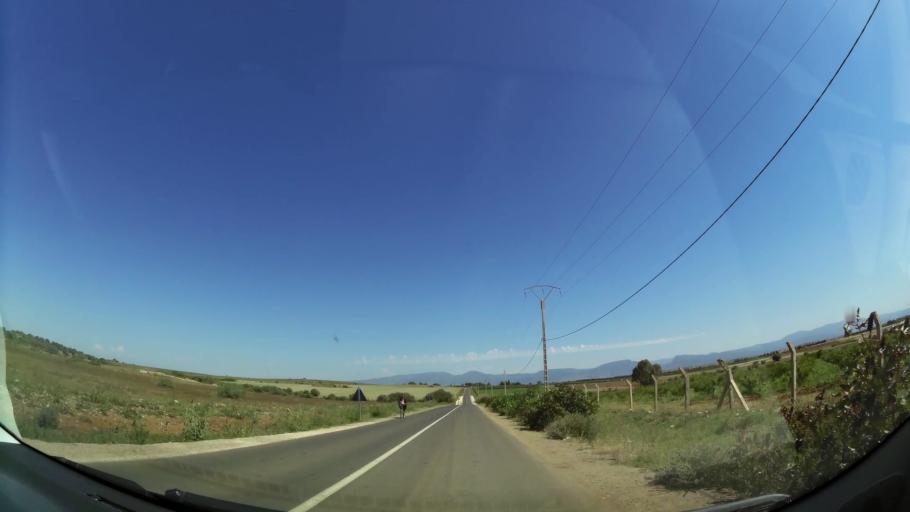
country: MA
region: Oriental
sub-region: Berkane-Taourirt
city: Madagh
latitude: 35.0350
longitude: -2.4185
